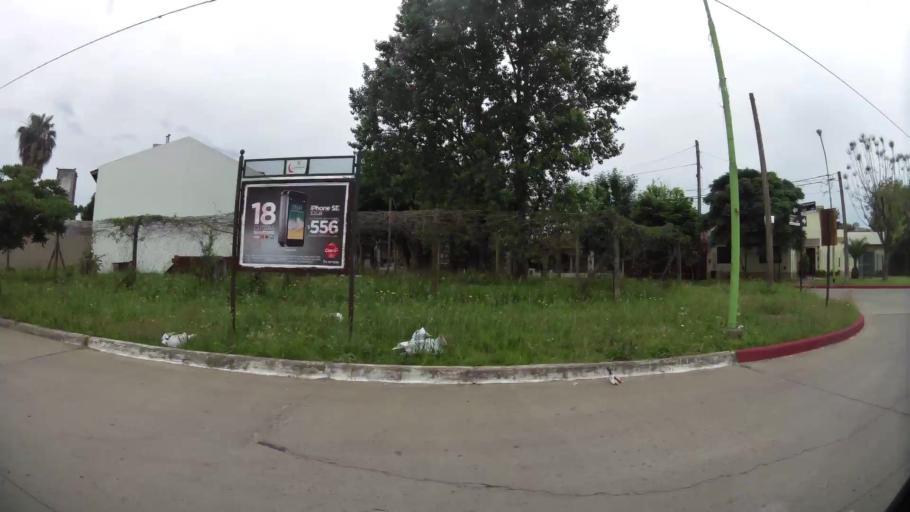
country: AR
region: Buenos Aires
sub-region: Partido de Campana
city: Campana
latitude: -34.1810
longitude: -58.9599
